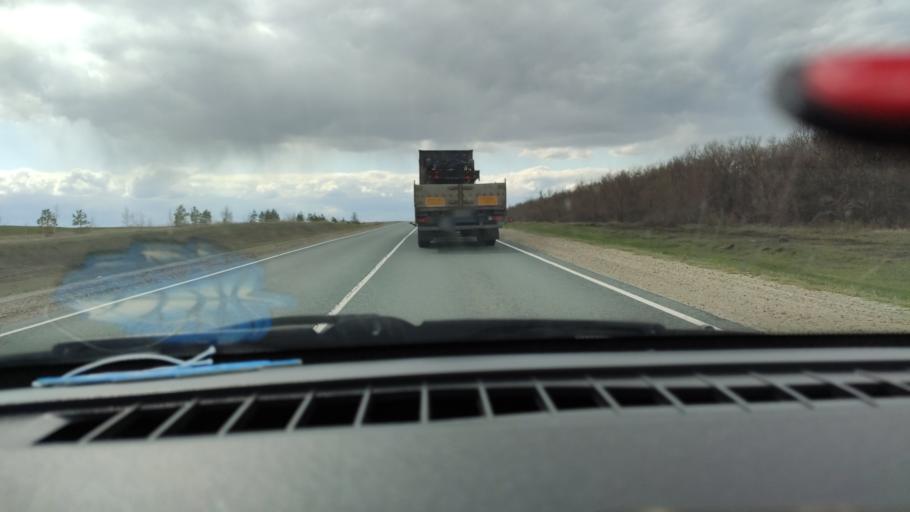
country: RU
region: Saratov
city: Alekseyevka
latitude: 52.2323
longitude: 47.9035
